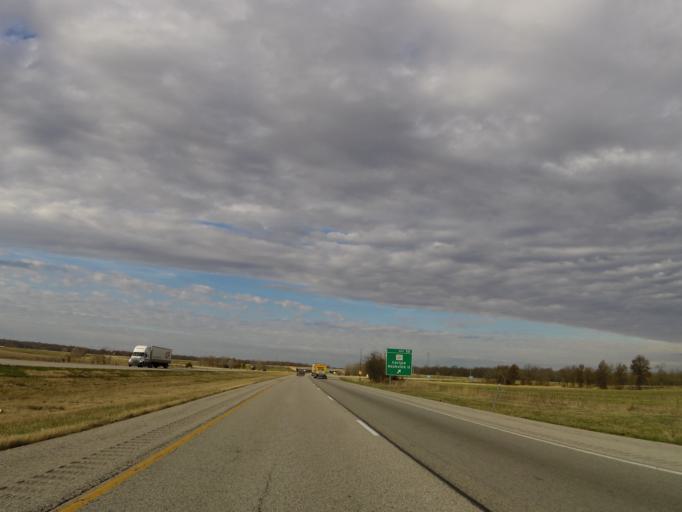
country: US
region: Illinois
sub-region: Washington County
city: Nashville
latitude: 38.3912
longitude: -89.3633
